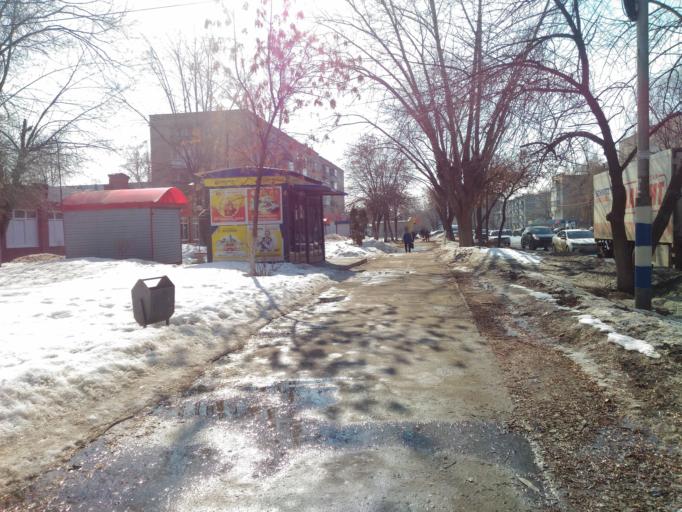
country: RU
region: Ulyanovsk
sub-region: Ulyanovskiy Rayon
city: Ulyanovsk
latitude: 54.3320
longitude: 48.4852
